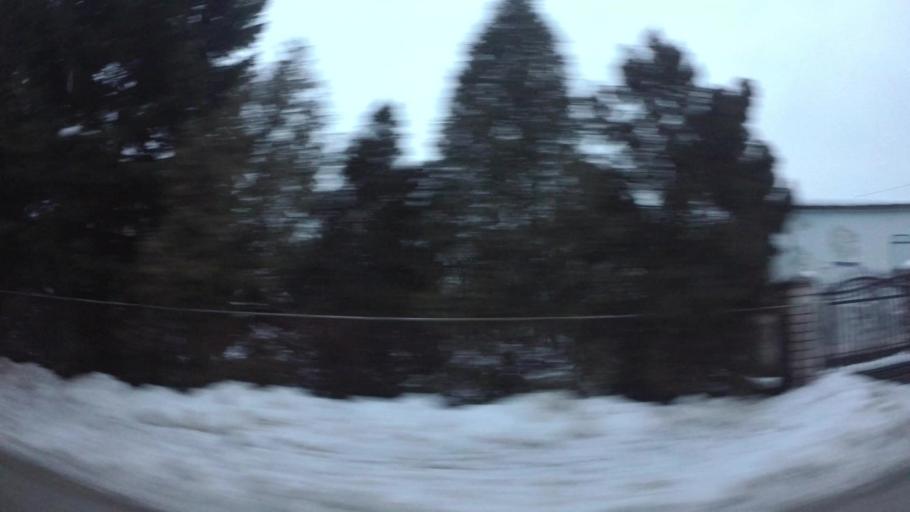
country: BA
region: Federation of Bosnia and Herzegovina
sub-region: Kanton Sarajevo
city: Sarajevo
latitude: 43.8526
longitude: 18.2961
